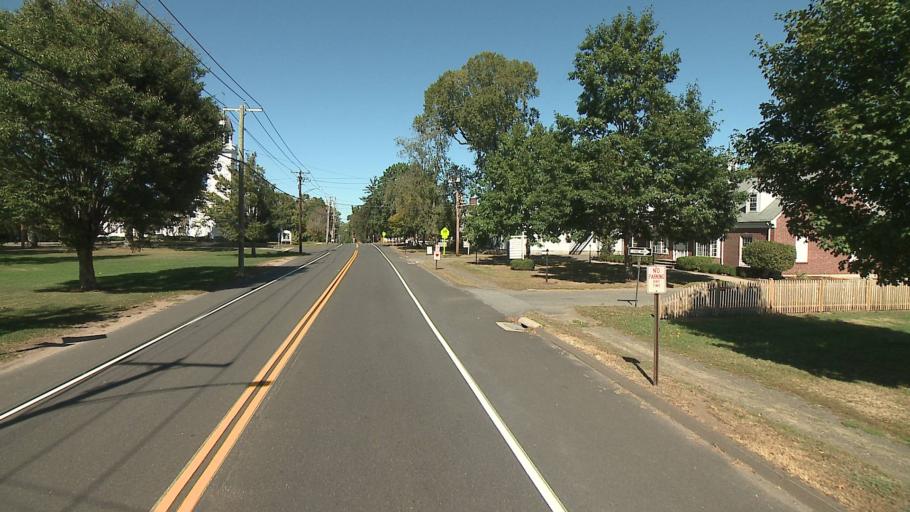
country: US
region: Connecticut
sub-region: New Haven County
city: Orange
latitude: 41.2778
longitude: -73.0254
